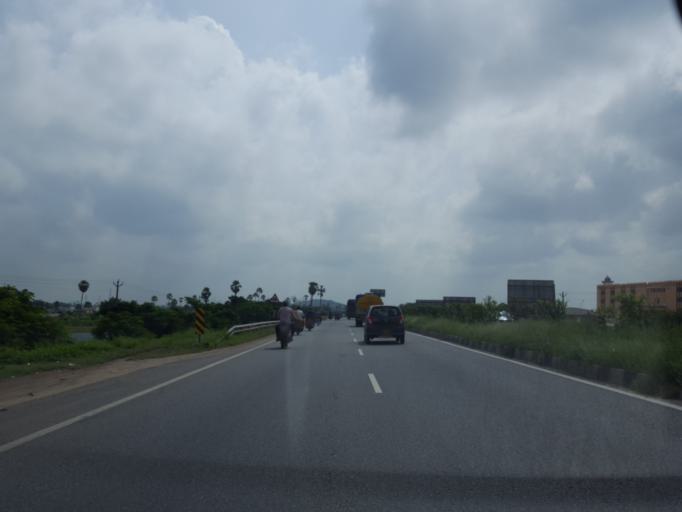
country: IN
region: Telangana
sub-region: Nalgonda
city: Bhongir
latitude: 17.2311
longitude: 78.9664
